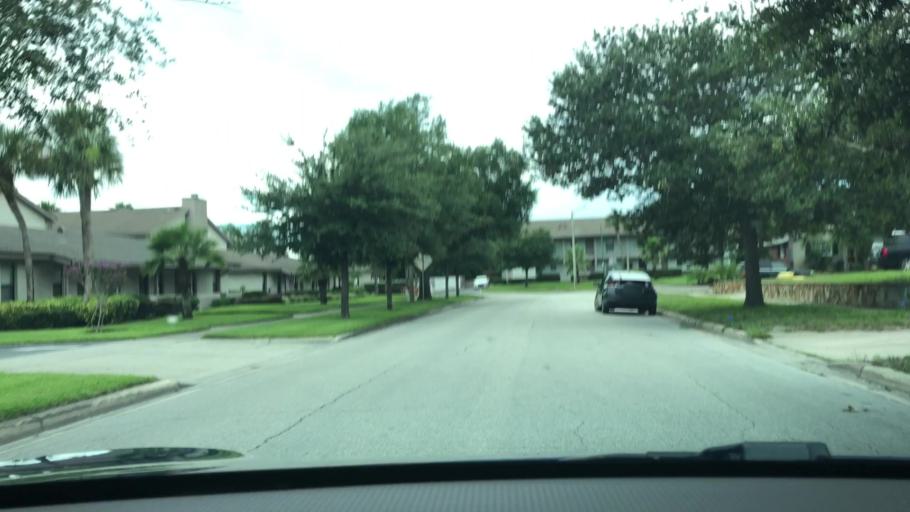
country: US
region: Florida
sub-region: Orange County
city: Winter Park
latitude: 28.5619
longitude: -81.3467
